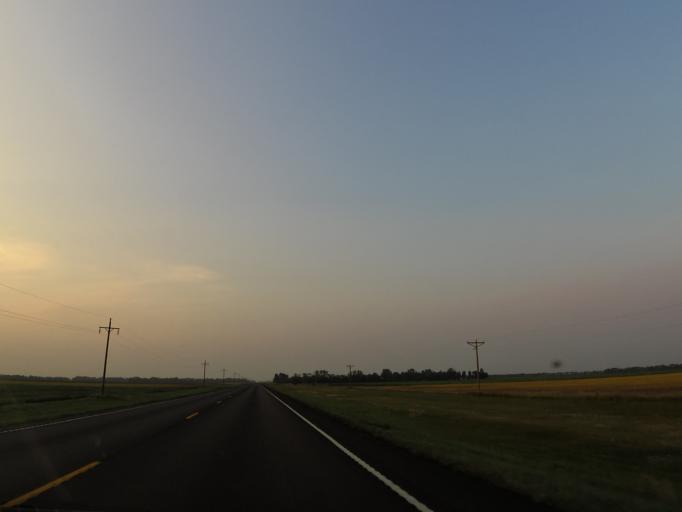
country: US
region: North Dakota
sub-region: Walsh County
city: Park River
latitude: 48.2759
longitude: -97.6223
